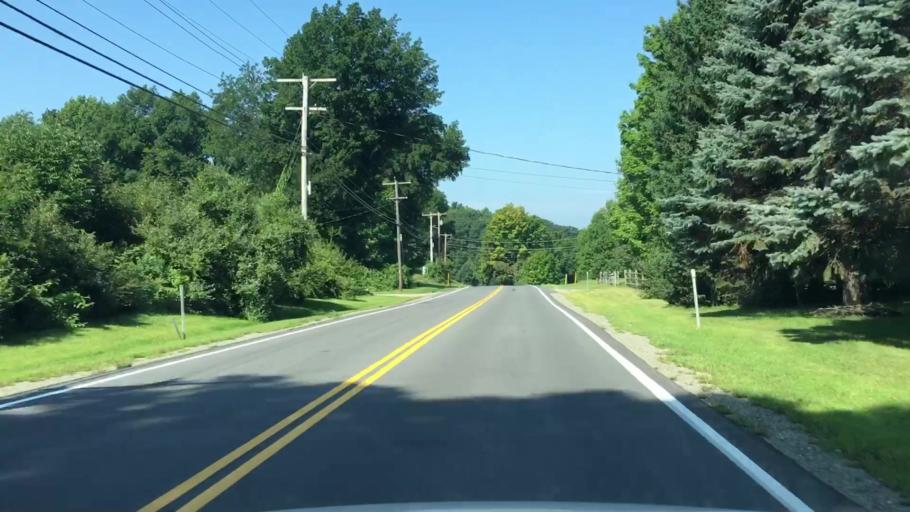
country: US
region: New Hampshire
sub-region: Rockingham County
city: East Kingston
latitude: 42.9226
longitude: -70.9990
